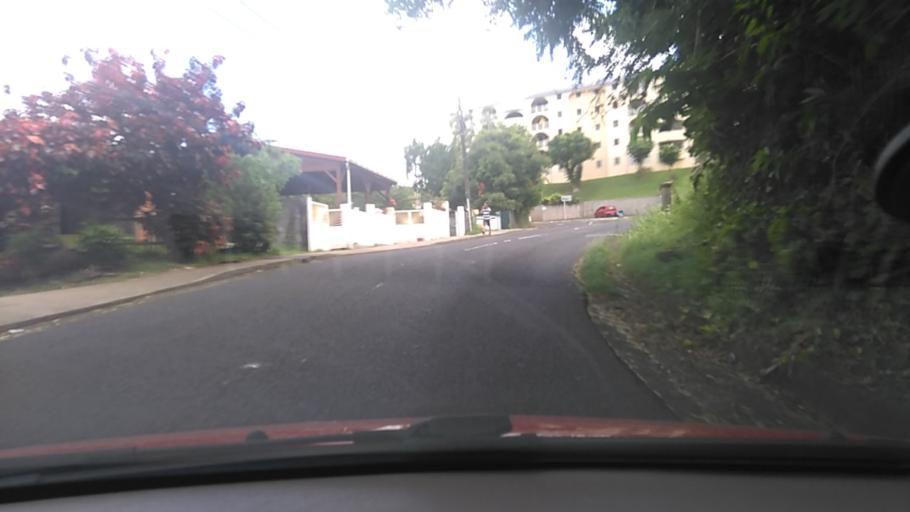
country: MQ
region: Martinique
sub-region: Martinique
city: Ducos
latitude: 14.5716
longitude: -60.9619
